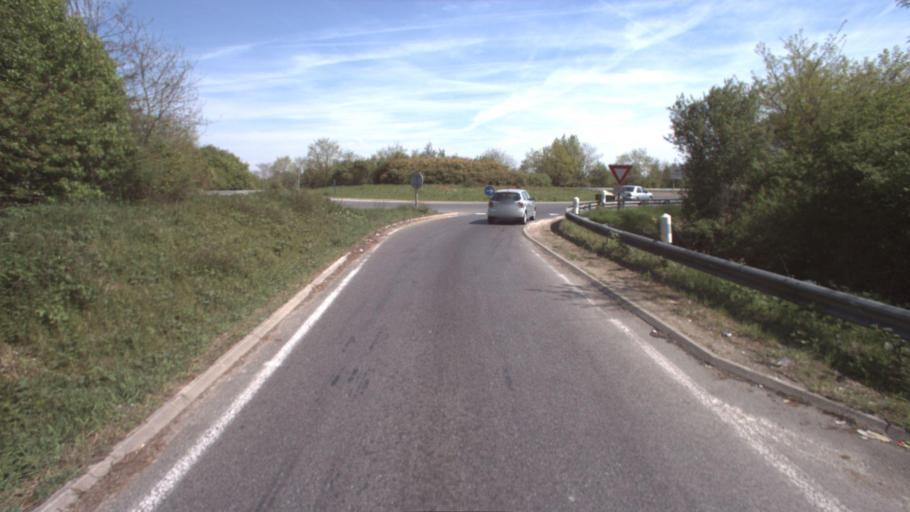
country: FR
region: Ile-de-France
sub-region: Departement de Seine-et-Marne
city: Saint-Mard
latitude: 49.0574
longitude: 2.7022
